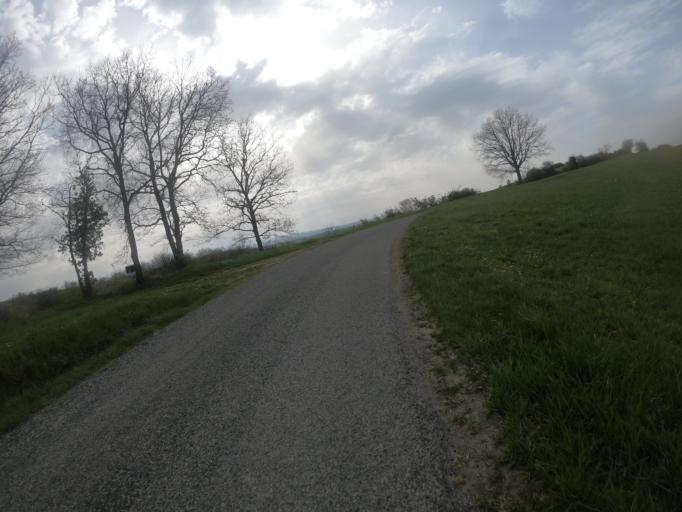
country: FR
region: Languedoc-Roussillon
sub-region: Departement de l'Aude
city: Belpech
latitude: 43.1297
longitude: 1.7611
